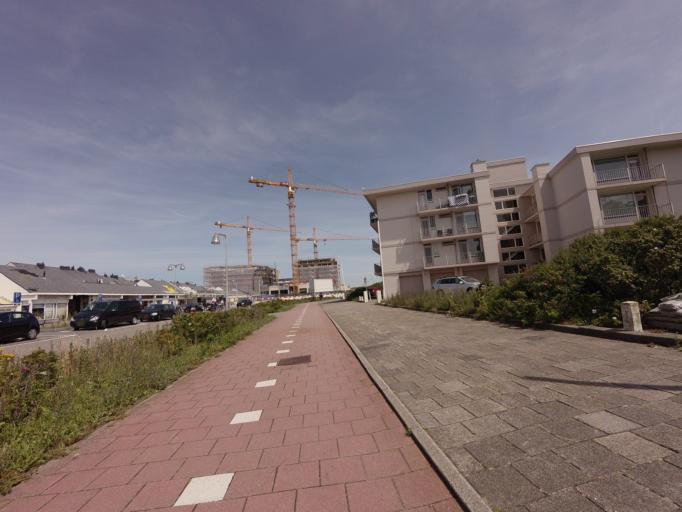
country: NL
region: South Holland
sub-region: Gemeente Westland
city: Poeldijk
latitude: 52.0676
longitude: 4.2199
